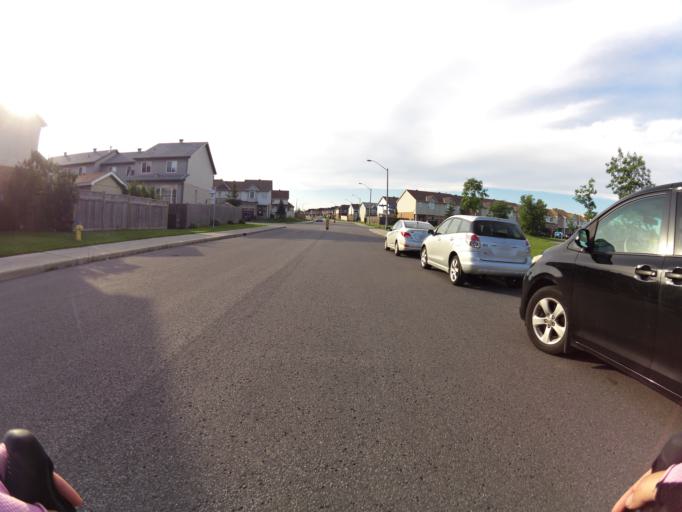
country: CA
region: Ontario
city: Bells Corners
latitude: 45.2678
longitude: -75.7776
